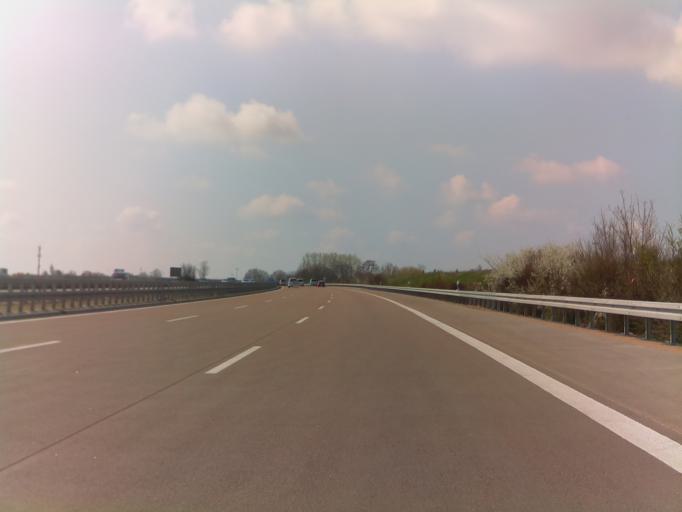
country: DE
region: Saxony-Anhalt
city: Granschutz
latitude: 51.2019
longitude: 12.0212
